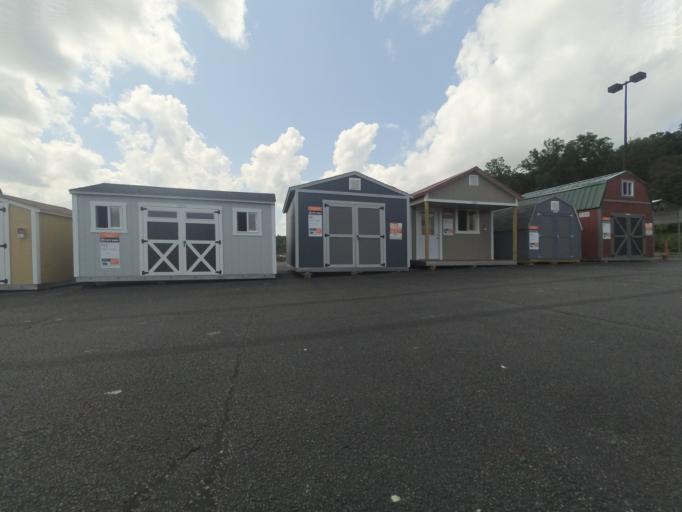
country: US
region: West Virginia
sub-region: Cabell County
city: Barboursville
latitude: 38.4224
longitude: -82.2868
